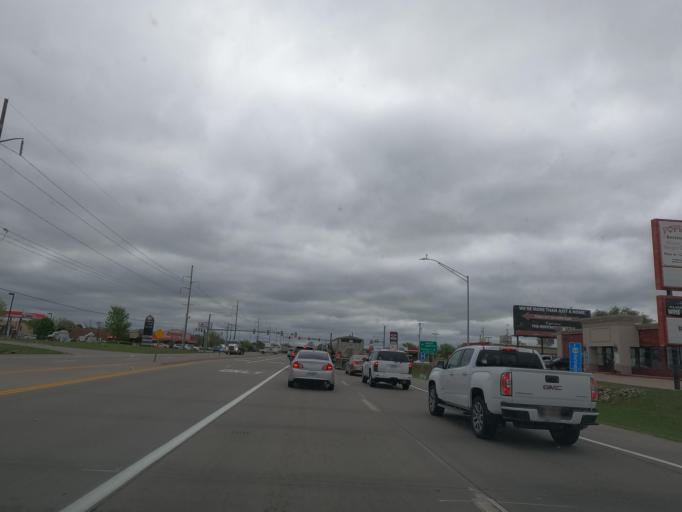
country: US
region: Kansas
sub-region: Butler County
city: Andover
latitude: 37.6796
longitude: -97.1369
